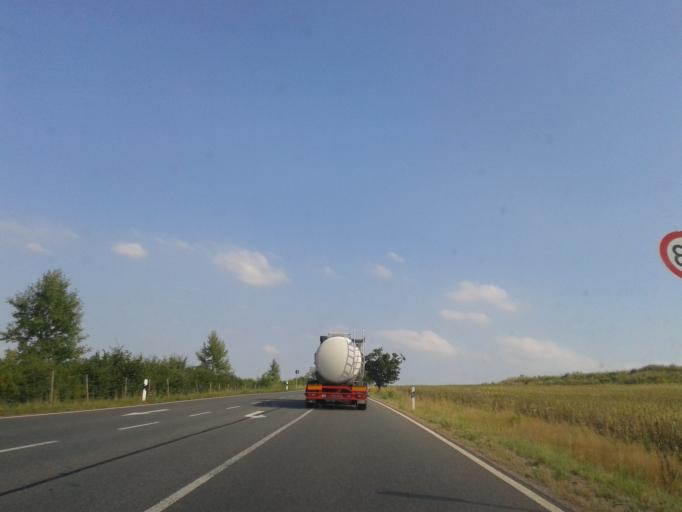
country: DE
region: Saxony
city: Wilsdruff
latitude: 51.0497
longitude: 13.5506
